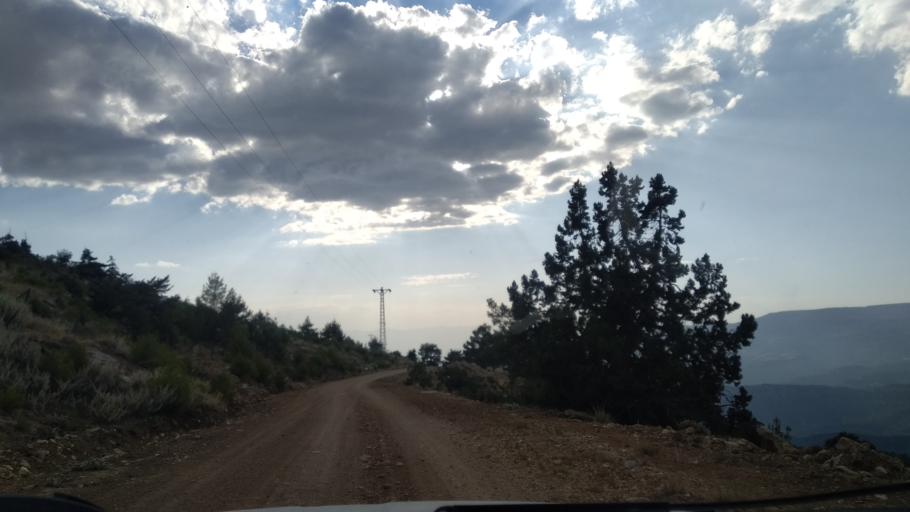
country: TR
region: Mersin
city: Sarikavak
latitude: 36.5978
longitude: 33.6936
